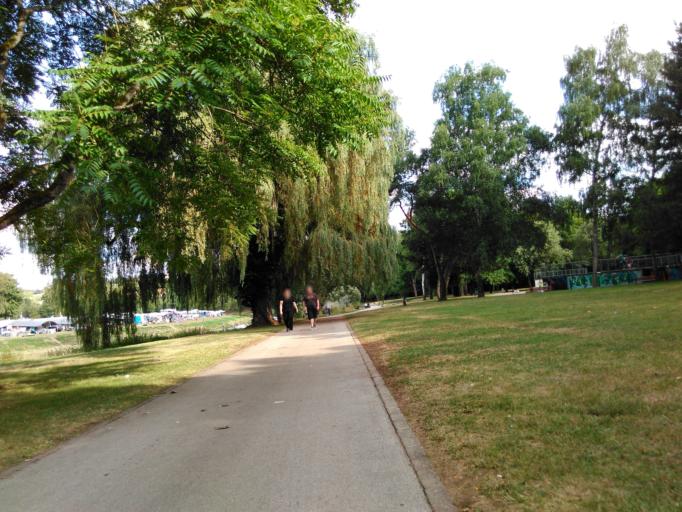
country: LU
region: Grevenmacher
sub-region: Canton d'Echternach
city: Echternach
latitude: 49.8121
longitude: 6.4262
